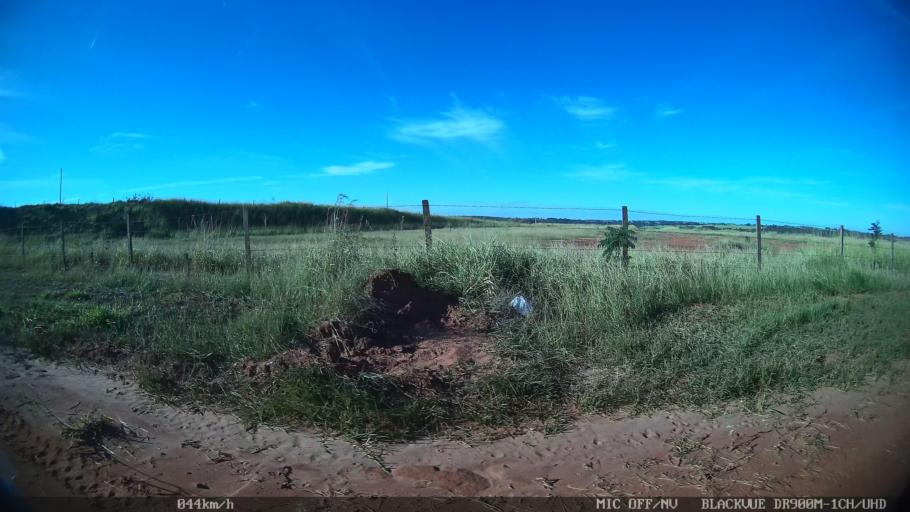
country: BR
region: Sao Paulo
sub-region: Sao Jose Do Rio Preto
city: Sao Jose do Rio Preto
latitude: -20.8781
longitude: -49.3188
